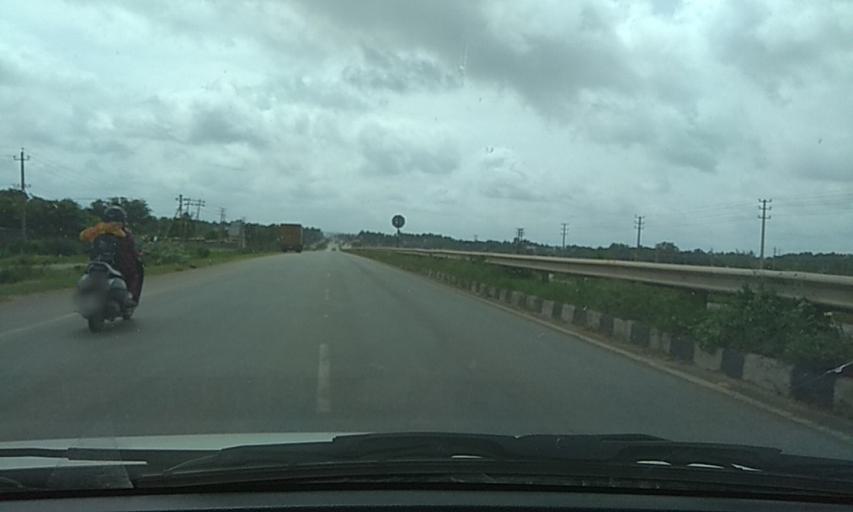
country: IN
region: Karnataka
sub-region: Davanagere
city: Harihar
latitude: 14.4544
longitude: 75.8694
